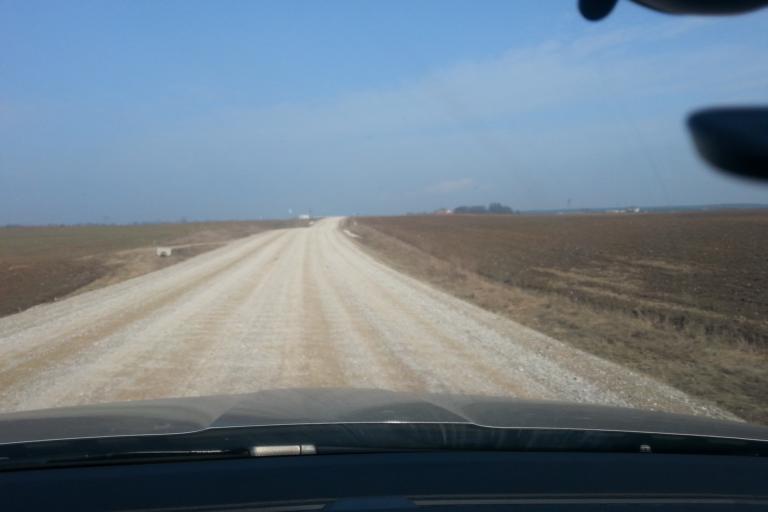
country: LT
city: Trakai
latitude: 54.5952
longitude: 24.9777
